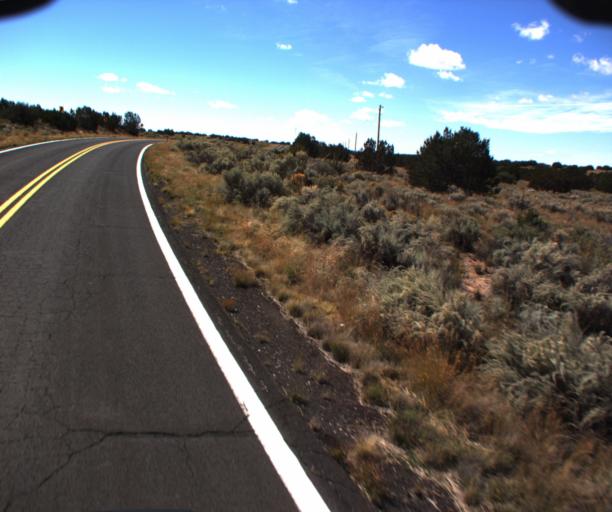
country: US
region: Arizona
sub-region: Apache County
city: Houck
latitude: 34.9278
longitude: -109.1998
